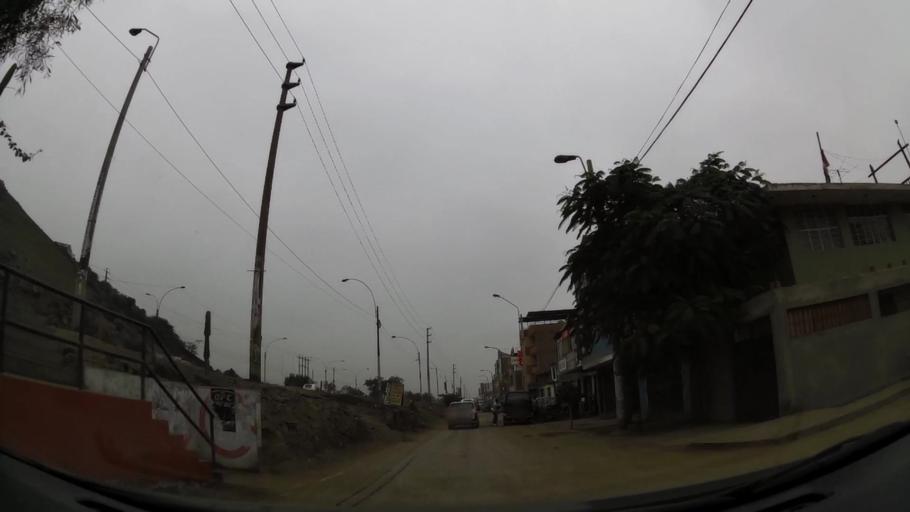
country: PE
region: Lima
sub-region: Lima
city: Urb. Santo Domingo
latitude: -11.9106
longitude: -77.0383
